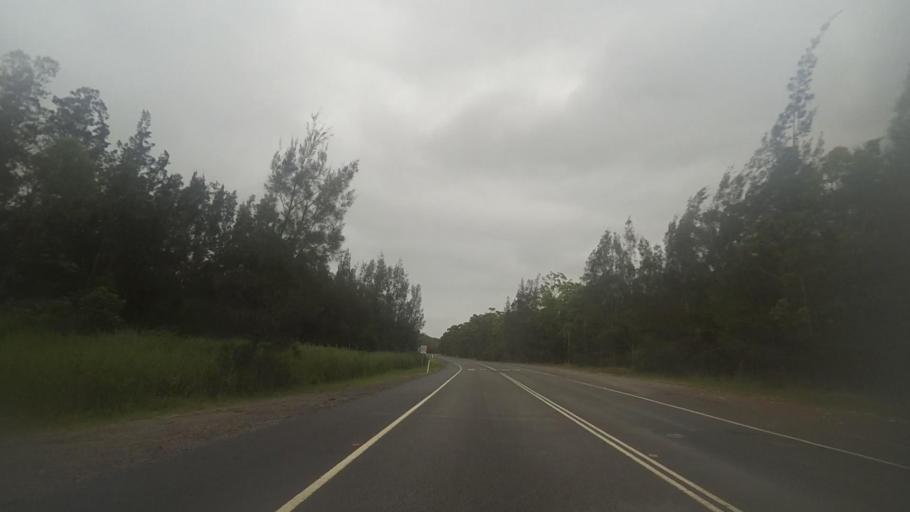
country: AU
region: New South Wales
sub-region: Port Stephens Shire
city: Port Stephens
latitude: -32.6341
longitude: 151.9955
